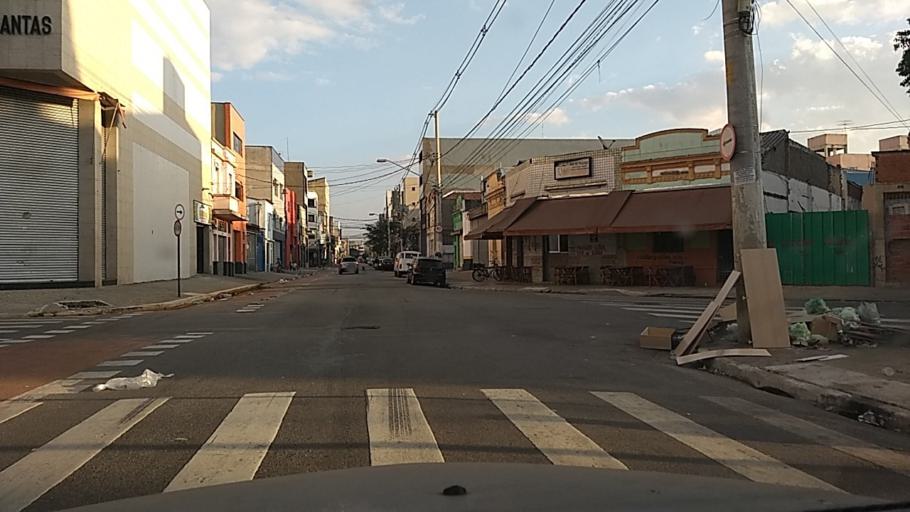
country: BR
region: Sao Paulo
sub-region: Sao Paulo
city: Sao Paulo
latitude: -23.5290
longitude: -46.6227
